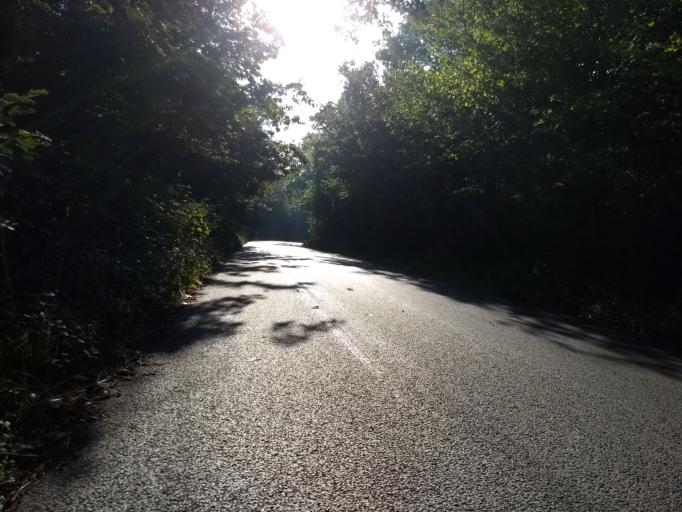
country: GB
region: England
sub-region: Isle of Wight
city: Newchurch
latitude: 50.7161
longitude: -1.2090
